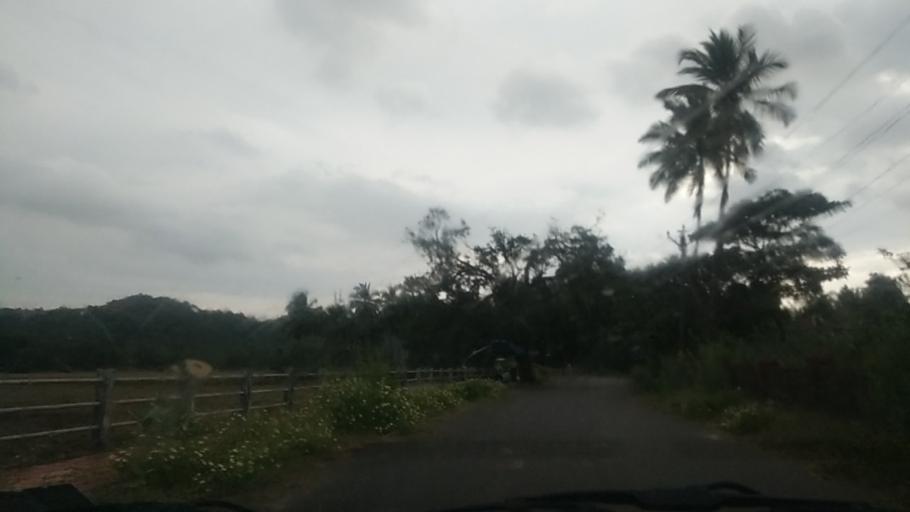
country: IN
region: Goa
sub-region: South Goa
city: Cuncolim
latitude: 15.1928
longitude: 73.9836
